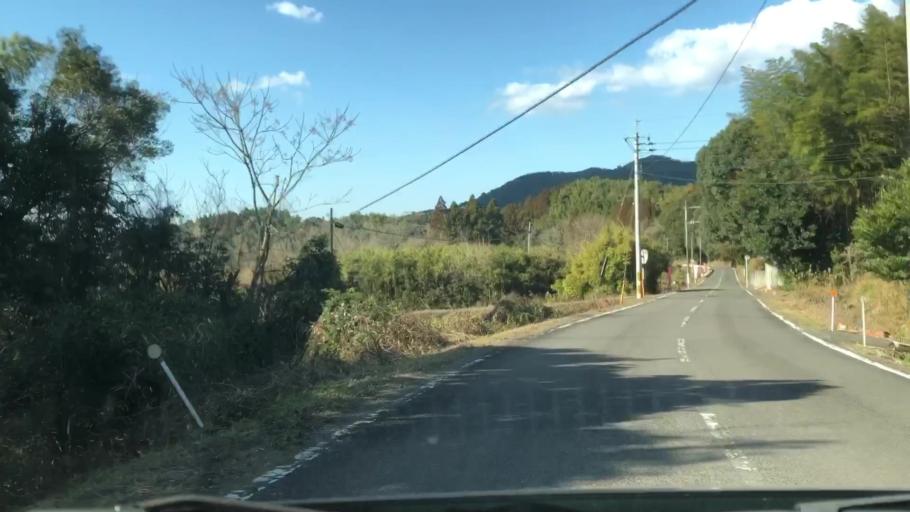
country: JP
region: Kagoshima
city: Satsumasendai
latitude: 31.8554
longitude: 130.3610
